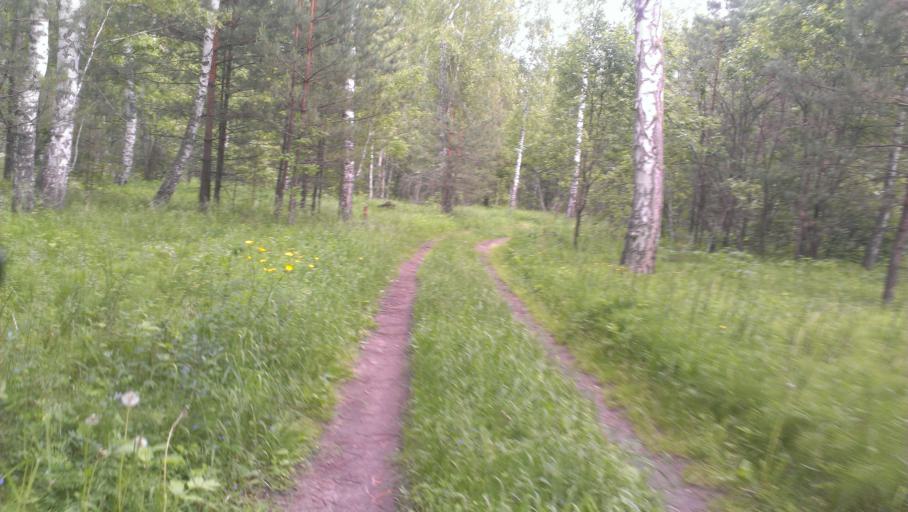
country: RU
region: Altai Krai
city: Sannikovo
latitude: 53.3494
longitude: 84.0329
